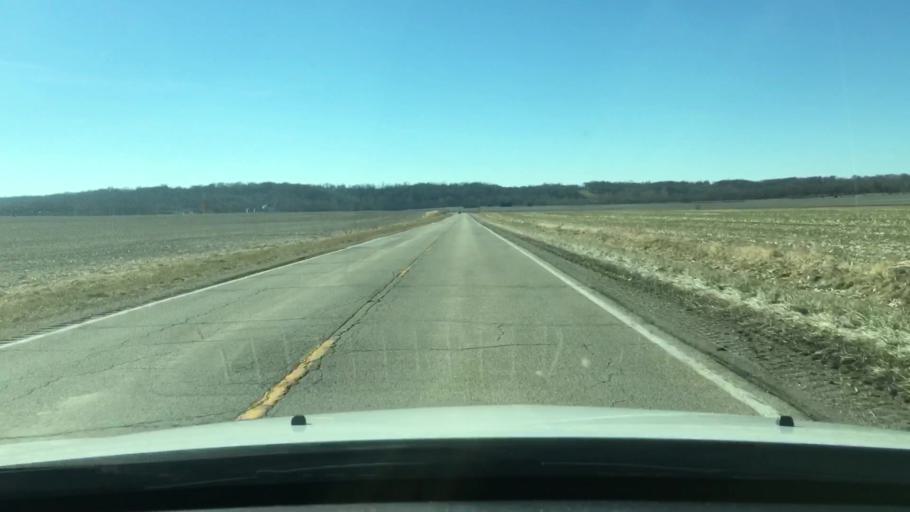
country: US
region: Illinois
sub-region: Mason County
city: Havana
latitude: 40.2824
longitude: -90.1661
